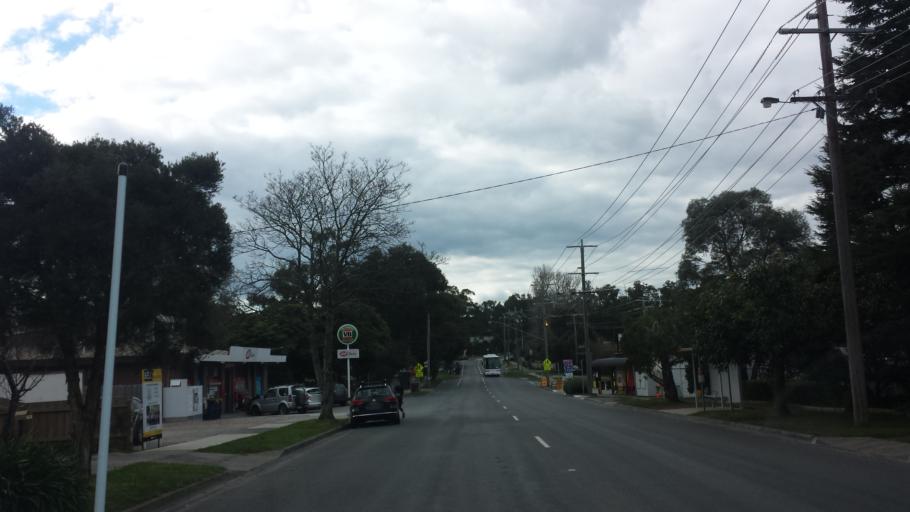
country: AU
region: Victoria
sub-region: Yarra Ranges
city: Belgrave Heights
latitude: -37.9322
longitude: 145.3580
